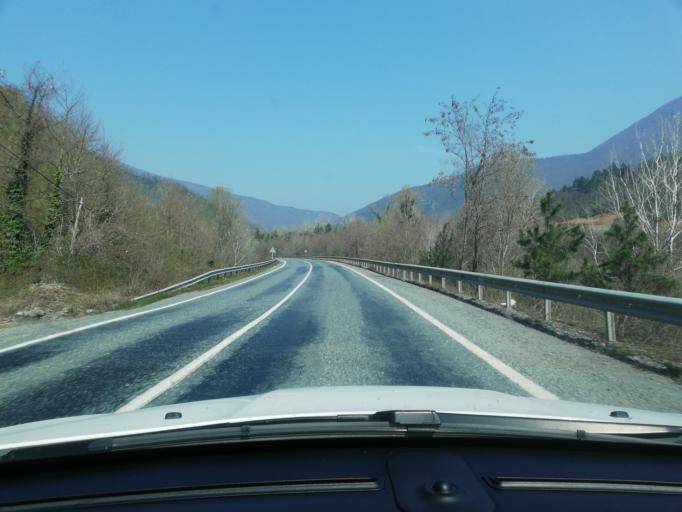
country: TR
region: Zonguldak
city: Gokcebey
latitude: 41.2419
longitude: 32.1703
